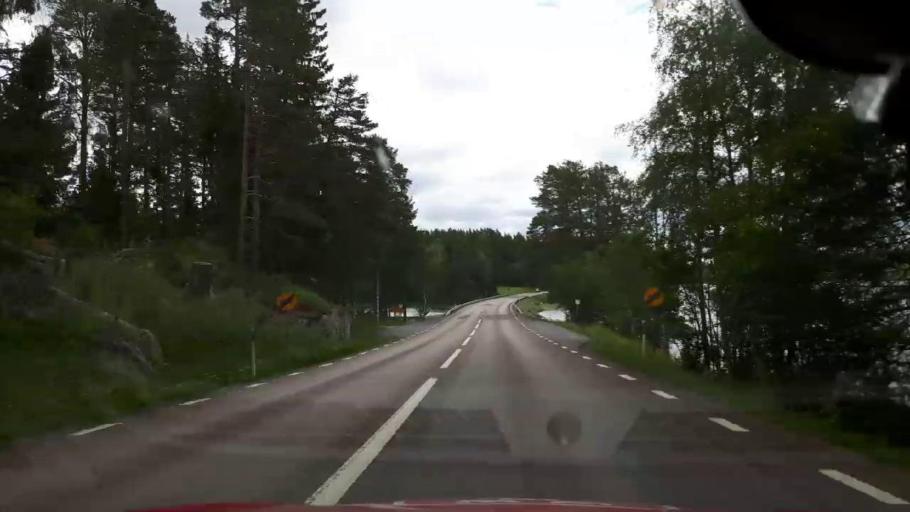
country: SE
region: Jaemtland
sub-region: OEstersunds Kommun
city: Brunflo
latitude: 63.0101
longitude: 14.9550
